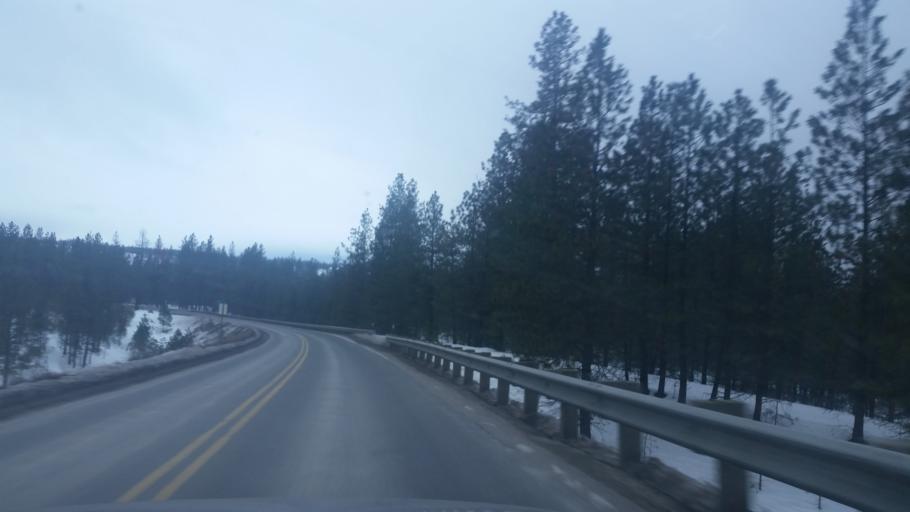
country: US
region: Washington
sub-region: Spokane County
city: Fairchild Air Force Base
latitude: 47.8500
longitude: -117.8533
